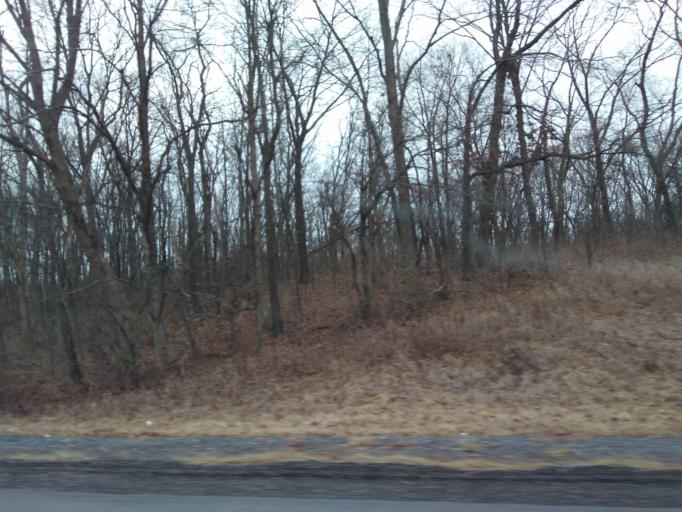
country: US
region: Illinois
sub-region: Madison County
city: Highland
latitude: 38.7863
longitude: -89.6923
